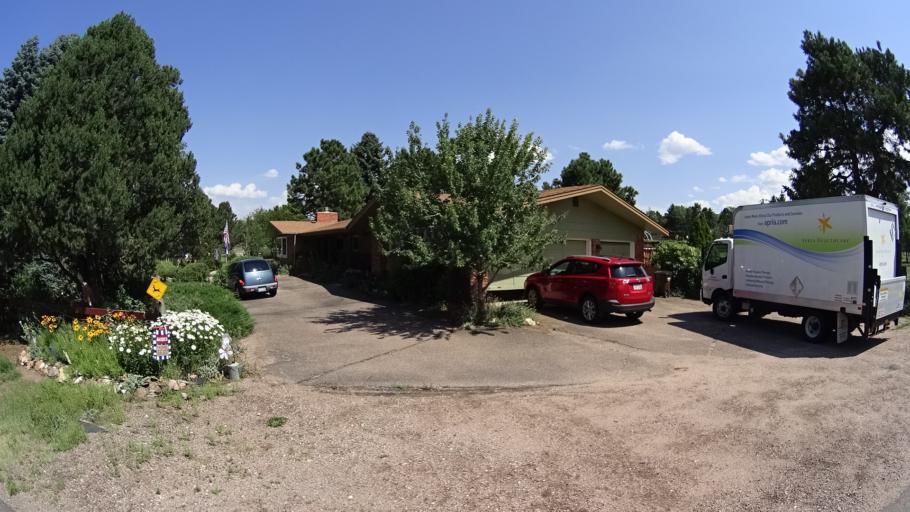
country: US
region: Colorado
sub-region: El Paso County
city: Air Force Academy
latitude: 38.9365
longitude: -104.7910
